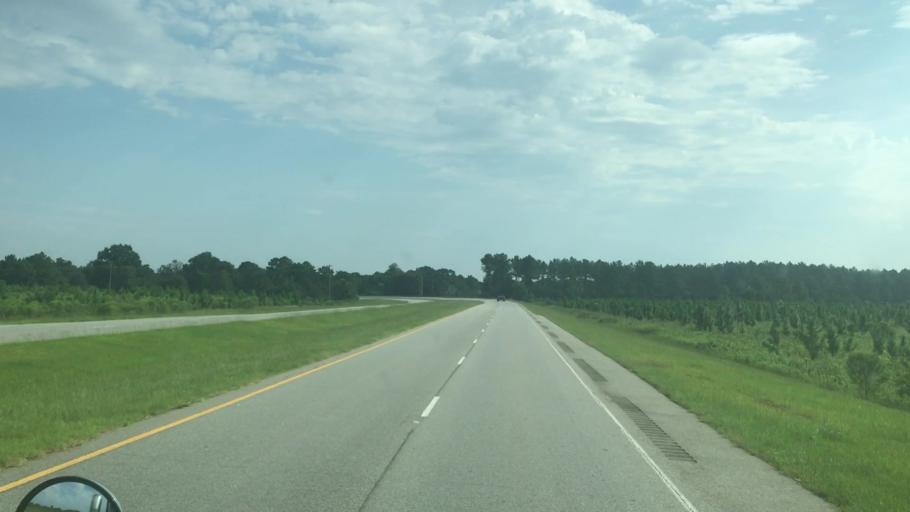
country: US
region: Georgia
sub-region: Early County
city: Blakely
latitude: 31.3625
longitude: -84.9222
